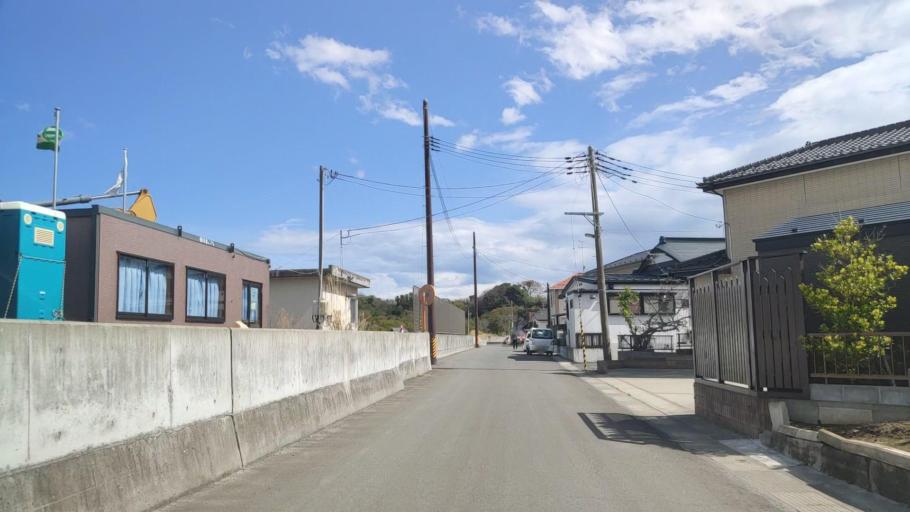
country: JP
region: Miyagi
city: Matsushima
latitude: 38.3397
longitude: 141.1447
